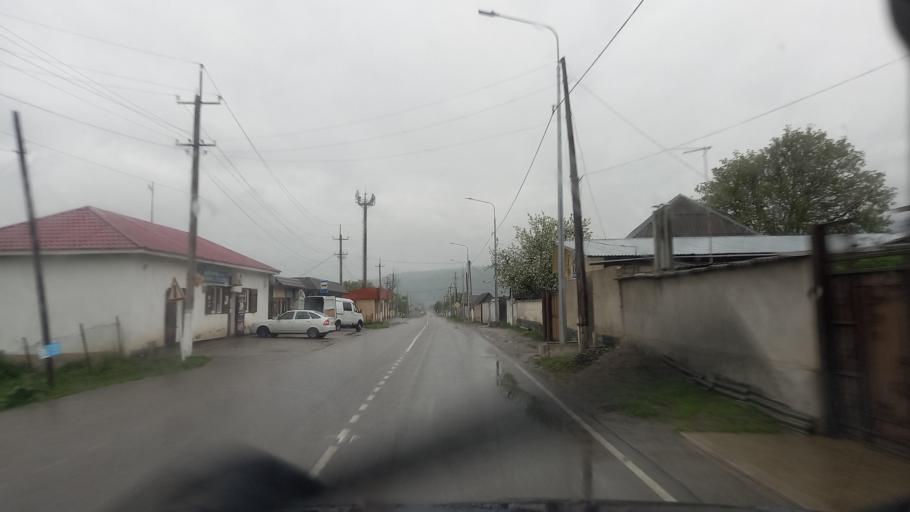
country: RU
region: Kabardino-Balkariya
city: Gundelen
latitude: 43.5898
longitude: 43.1968
